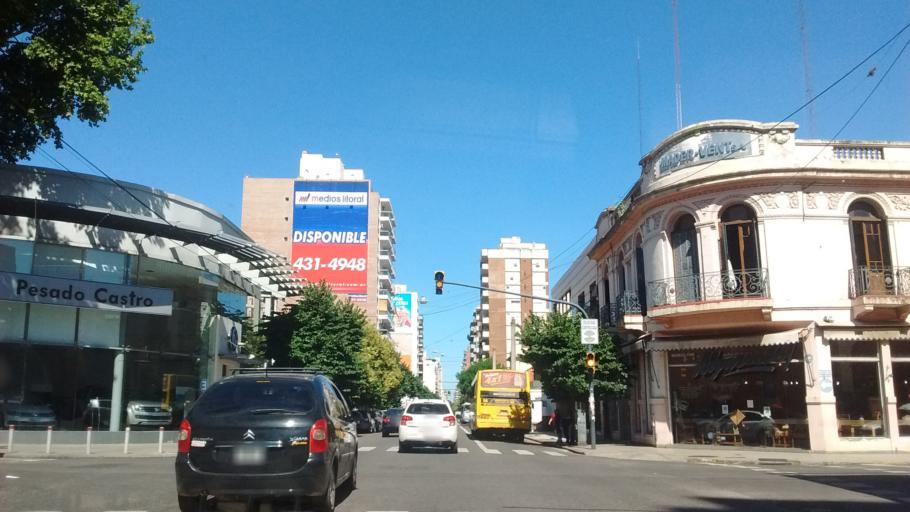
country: AR
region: Santa Fe
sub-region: Departamento de Rosario
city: Rosario
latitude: -32.9420
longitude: -60.6630
